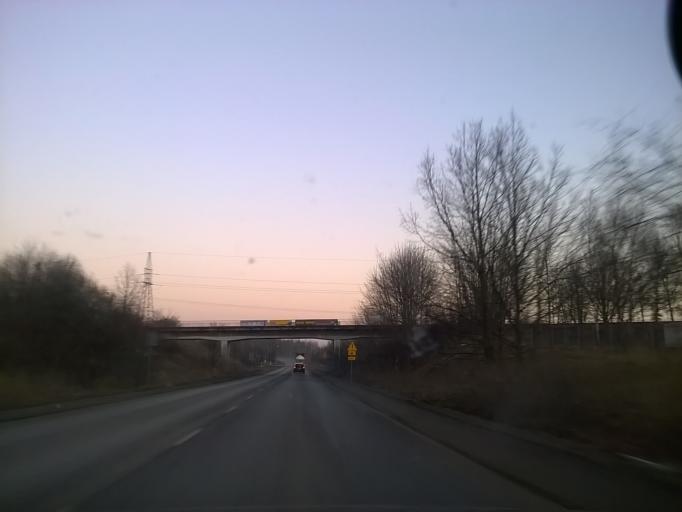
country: PL
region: Warmian-Masurian Voivodeship
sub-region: Powiat olsztynski
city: Olsztyn
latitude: 53.7816
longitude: 20.5465
